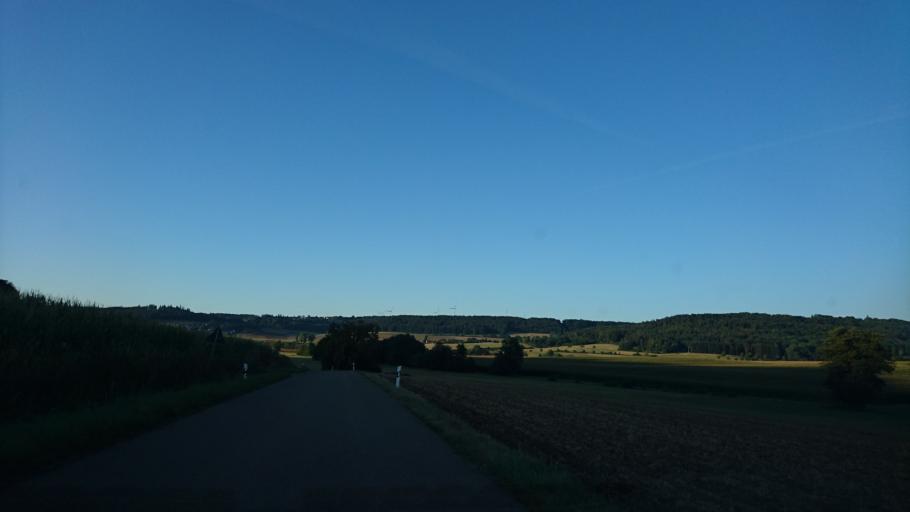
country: DE
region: Bavaria
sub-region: Regierungsbezirk Mittelfranken
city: Thalmassing
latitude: 49.0944
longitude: 11.2430
